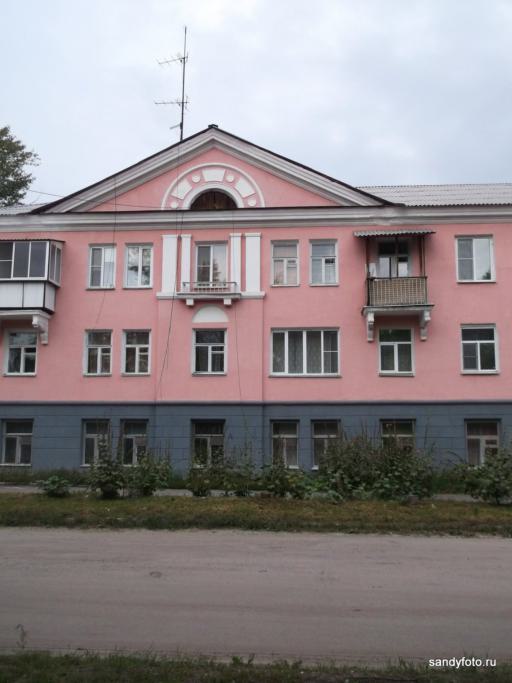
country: RU
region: Chelyabinsk
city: Troitsk
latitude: 54.0427
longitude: 61.6316
